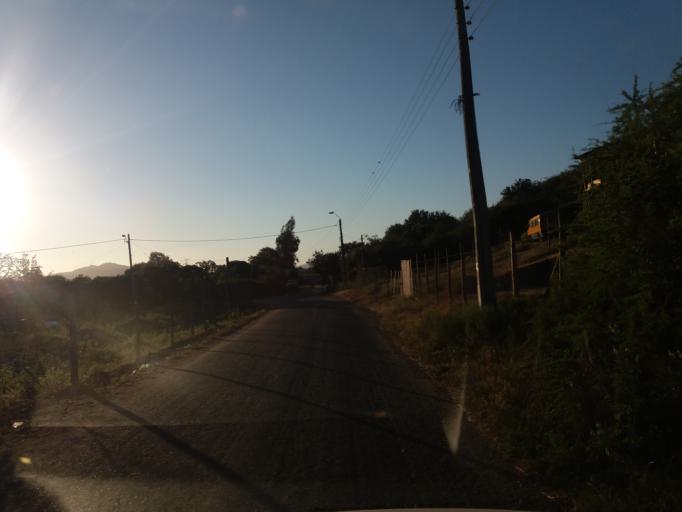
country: CL
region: Valparaiso
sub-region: Provincia de Quillota
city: Quillota
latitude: -32.9451
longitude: -71.2732
